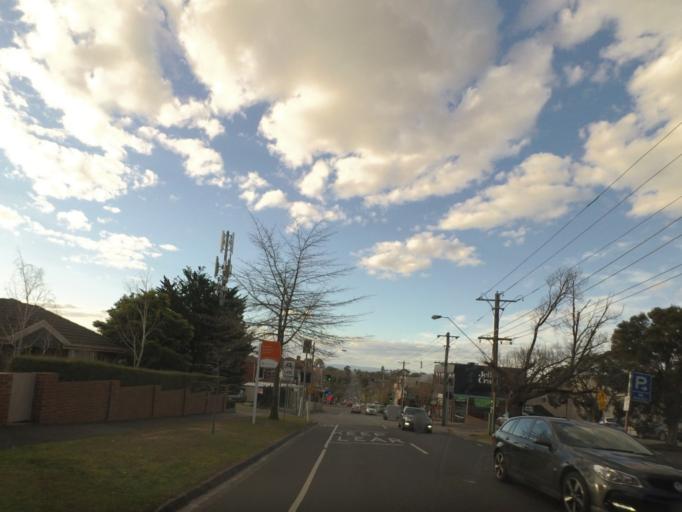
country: AU
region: Victoria
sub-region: Boroondara
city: Canterbury
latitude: -37.8136
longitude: 145.0812
